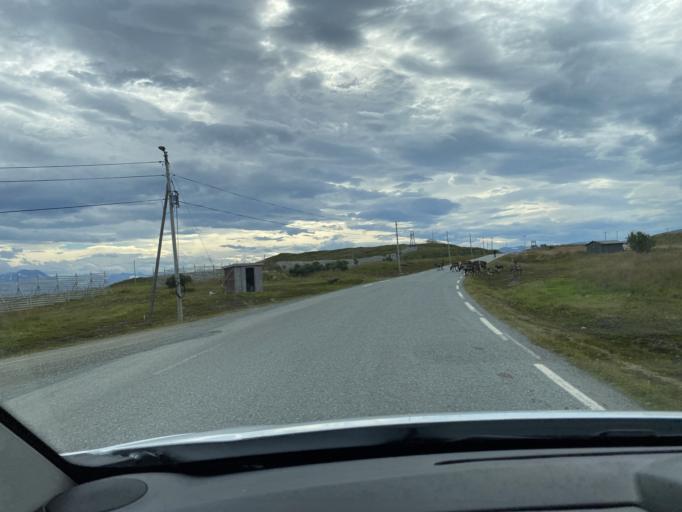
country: NO
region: Troms
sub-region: Karlsoy
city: Hansnes
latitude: 70.1011
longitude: 20.1077
